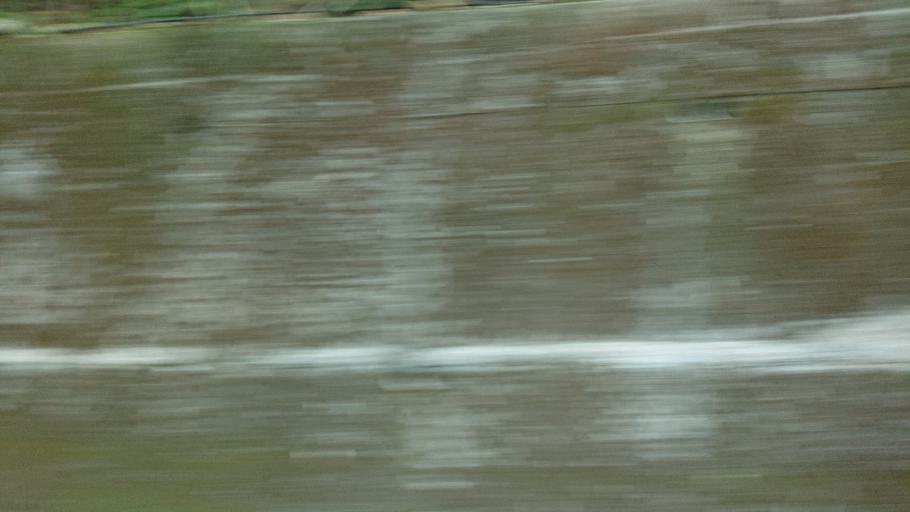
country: TW
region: Taiwan
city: Daxi
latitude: 24.8662
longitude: 121.4213
